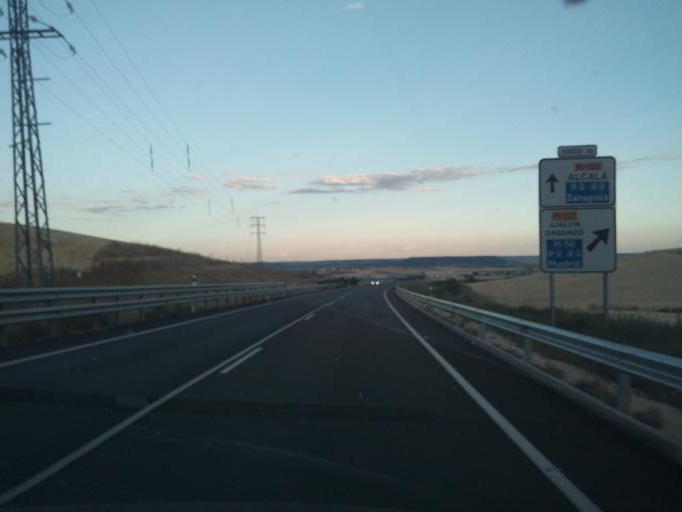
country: ES
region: Madrid
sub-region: Provincia de Madrid
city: Ajalvir
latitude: 40.5516
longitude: -3.4775
